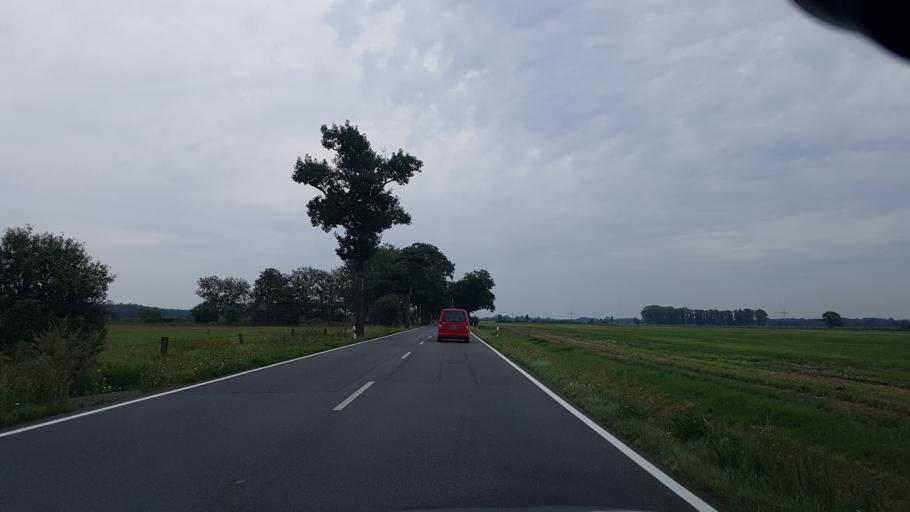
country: DE
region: Brandenburg
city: Plessa
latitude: 51.4692
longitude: 13.6655
